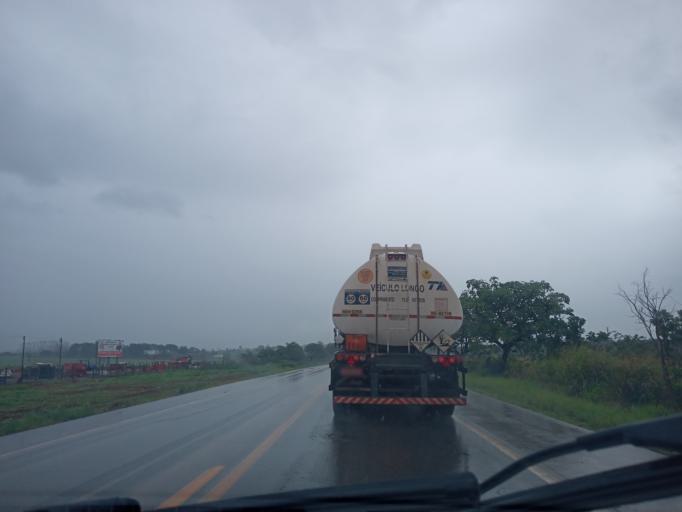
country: BR
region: Minas Gerais
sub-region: Luz
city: Luz
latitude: -19.7834
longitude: -45.6925
